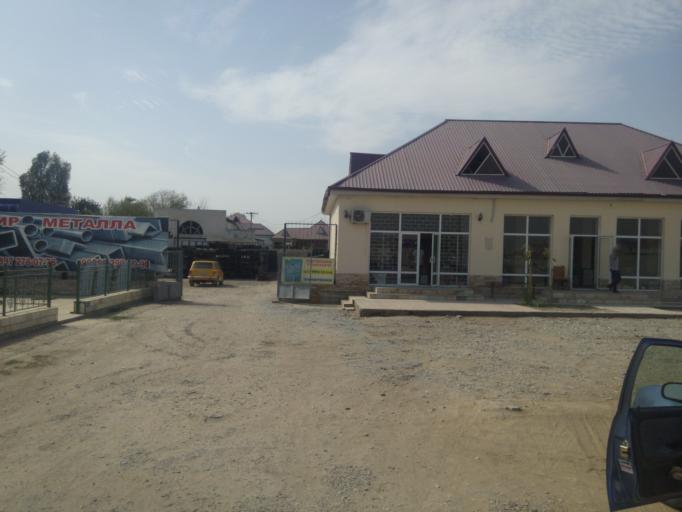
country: UZ
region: Sirdaryo
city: Guliston
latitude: 40.4943
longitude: 68.7976
